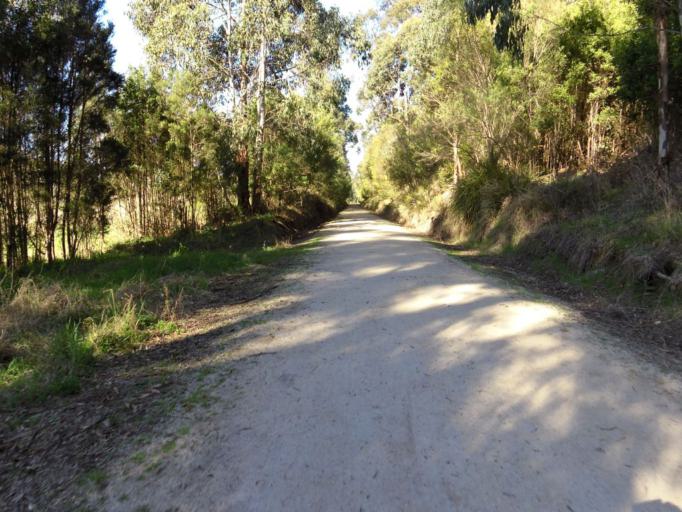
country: AU
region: Victoria
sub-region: Latrobe
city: Morwell
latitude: -38.3827
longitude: 146.2603
